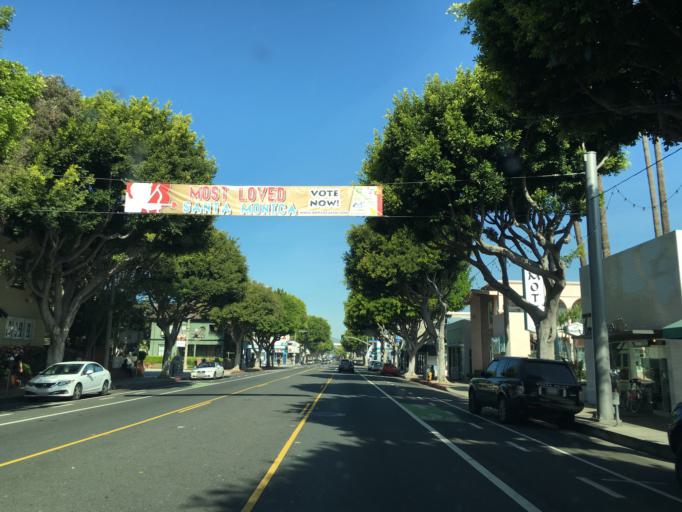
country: US
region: California
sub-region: Los Angeles County
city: Santa Monica
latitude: 34.0014
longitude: -118.4829
